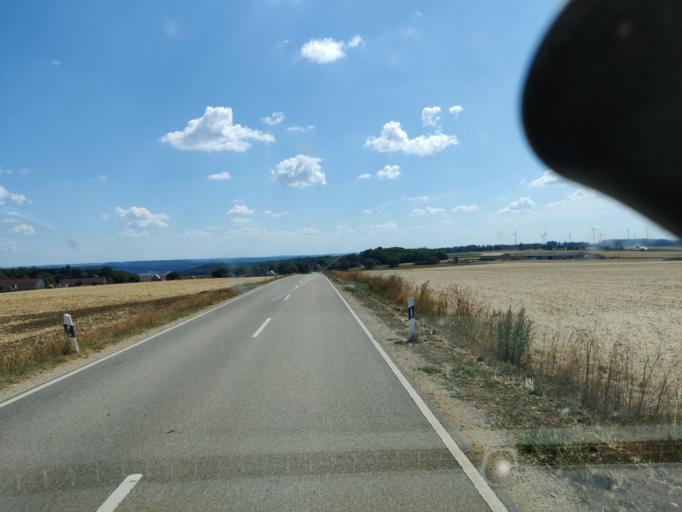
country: DE
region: Bavaria
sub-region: Regierungsbezirk Mittelfranken
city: Thalmassing
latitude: 49.0777
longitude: 11.1783
